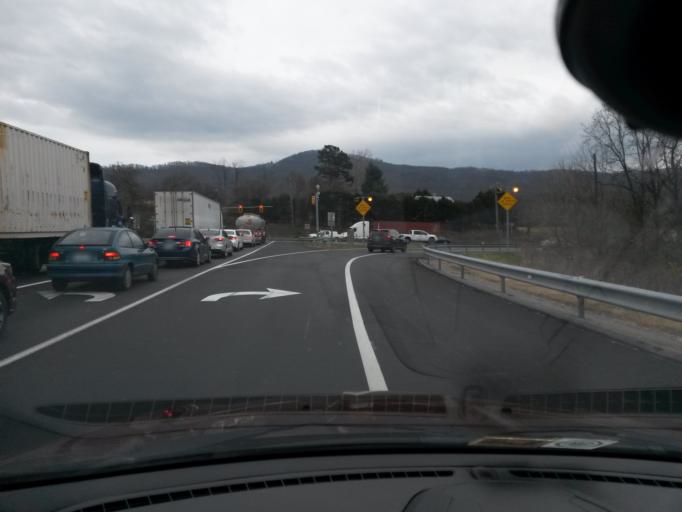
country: US
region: Virginia
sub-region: Botetourt County
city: Laymantown
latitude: 37.3257
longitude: -79.8700
